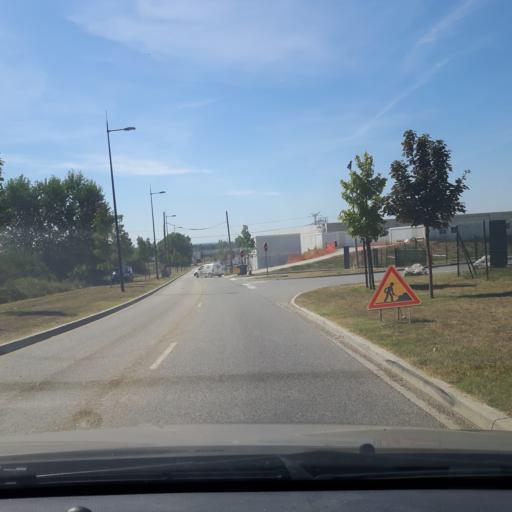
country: FR
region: Midi-Pyrenees
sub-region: Departement de la Haute-Garonne
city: Bouloc
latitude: 43.7688
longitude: 1.3908
